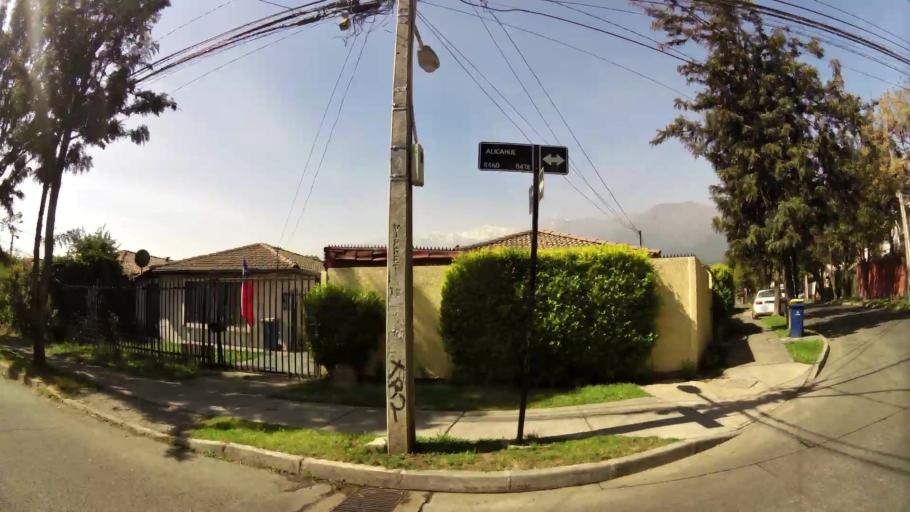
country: CL
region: Santiago Metropolitan
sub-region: Provincia de Santiago
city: Villa Presidente Frei, Nunoa, Santiago, Chile
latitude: -33.5309
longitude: -70.5674
